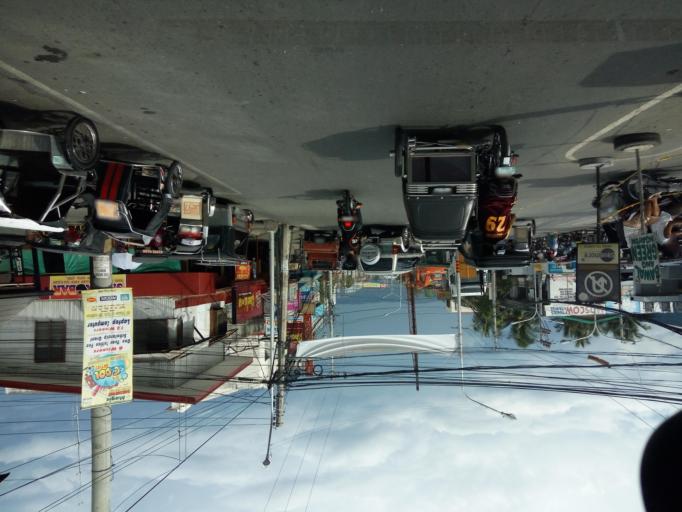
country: PH
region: Central Luzon
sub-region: Province of Nueva Ecija
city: Sibul
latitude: 15.7943
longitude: 120.9920
